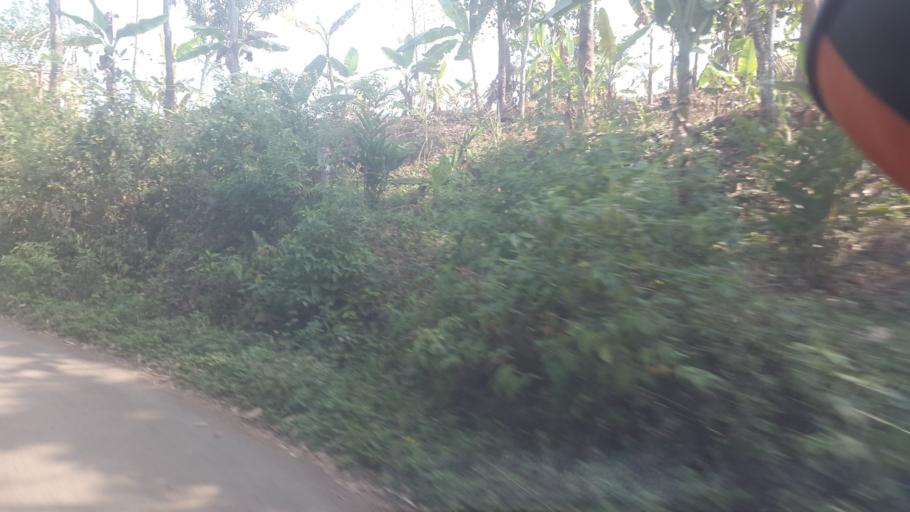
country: ID
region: West Java
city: Cijapar
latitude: -6.8990
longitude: 106.4318
